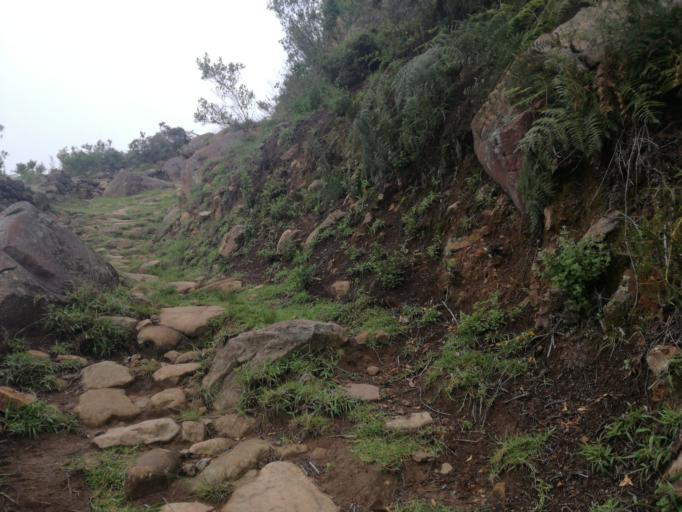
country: CO
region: Boyaca
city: Socha Viejo
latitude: 6.0016
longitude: -72.6855
